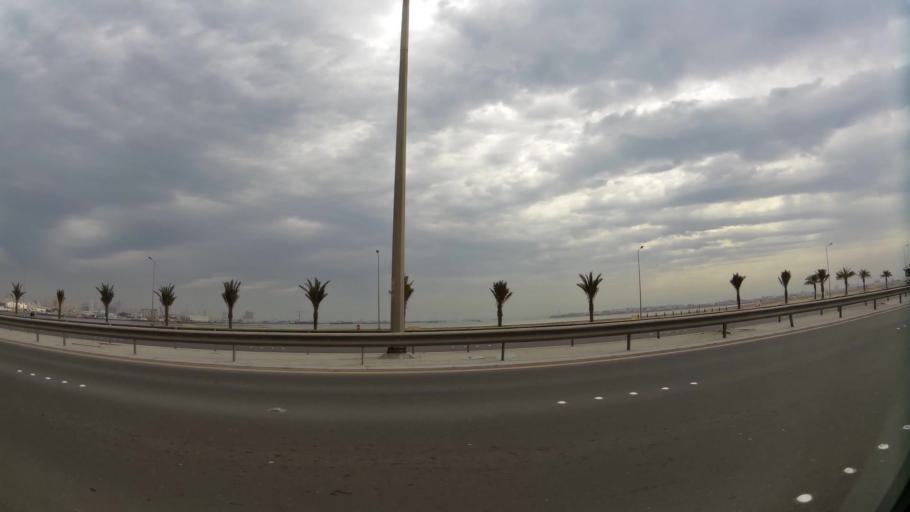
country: BH
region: Manama
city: Manama
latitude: 26.1868
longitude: 50.5894
